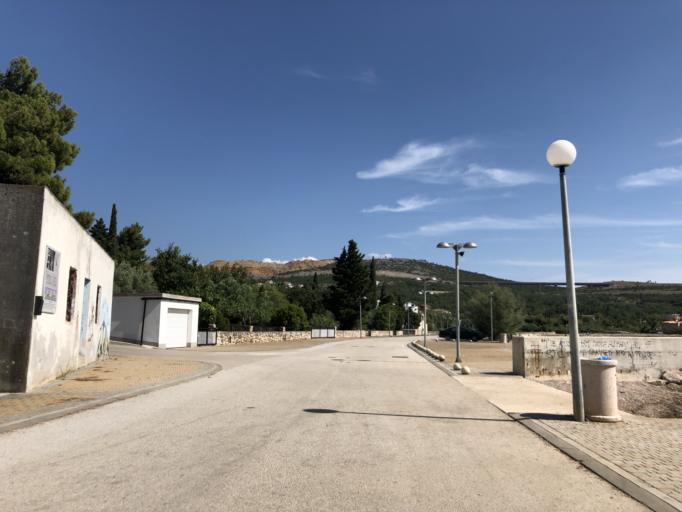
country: HR
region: Zadarska
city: Posedarje
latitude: 44.2502
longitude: 15.5374
